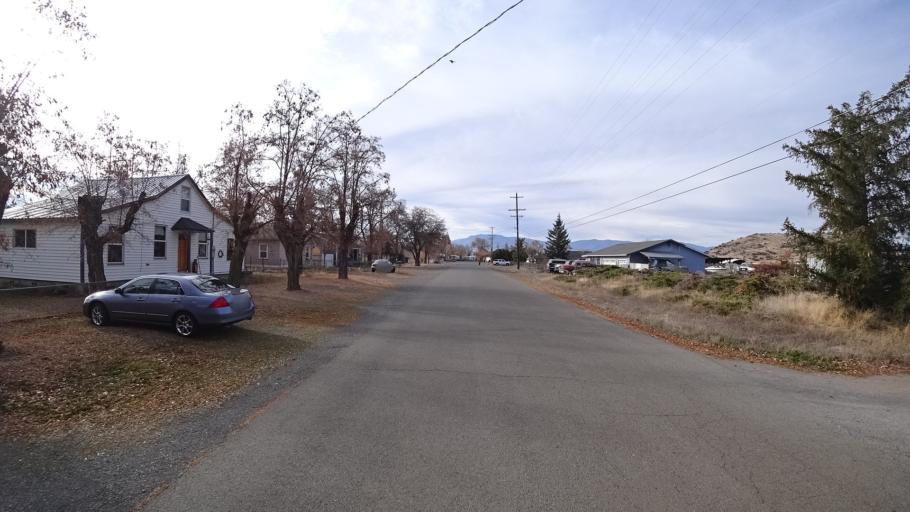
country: US
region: California
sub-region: Siskiyou County
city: Montague
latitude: 41.7297
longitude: -122.5332
